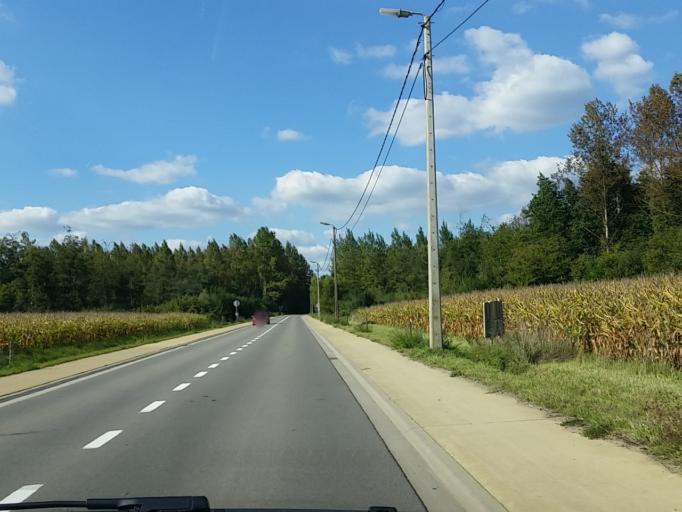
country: BE
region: Flanders
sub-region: Provincie Vlaams-Brabant
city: Holsbeek
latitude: 50.9256
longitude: 4.7507
